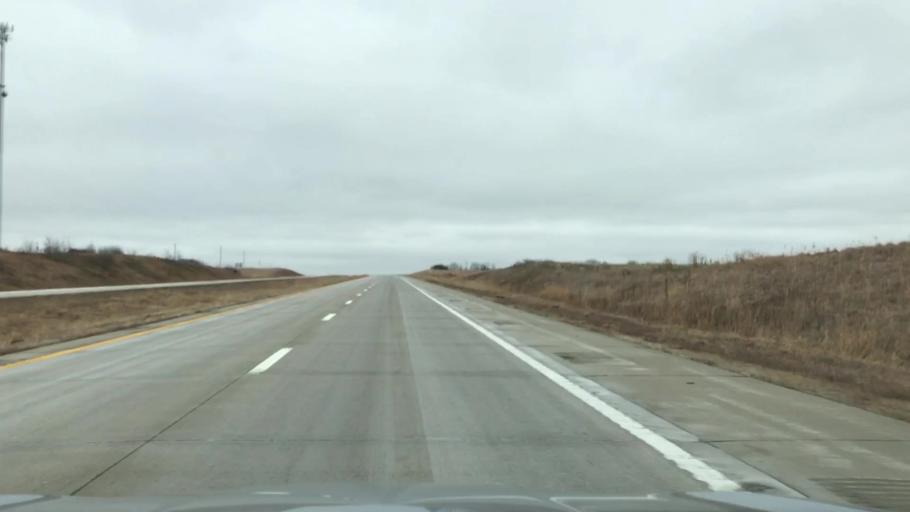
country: US
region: Missouri
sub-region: Caldwell County
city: Hamilton
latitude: 39.7348
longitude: -93.7721
